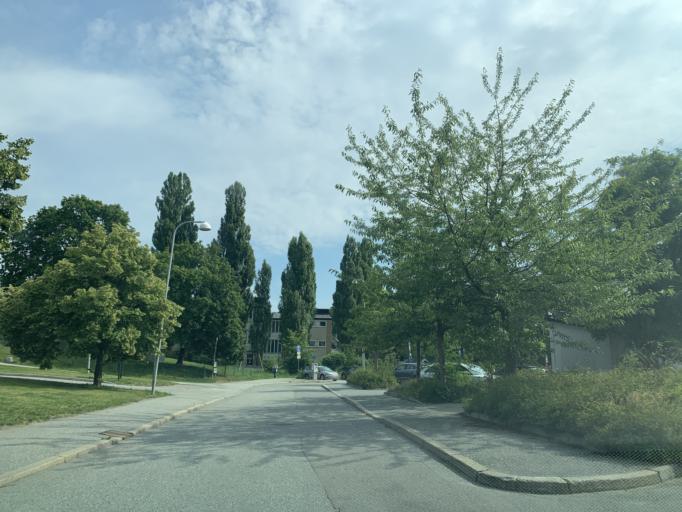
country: SE
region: Stockholm
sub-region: Norrtalje Kommun
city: Bergshamra
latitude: 59.3837
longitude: 18.0290
